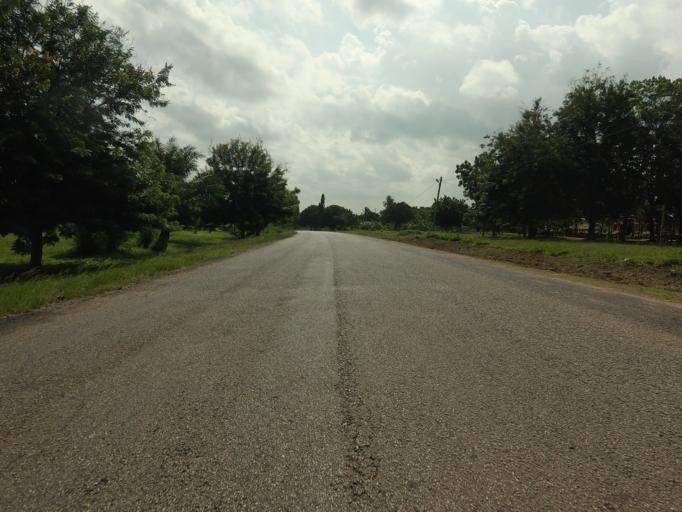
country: GH
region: Volta
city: Ho
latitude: 6.4155
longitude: 0.7548
